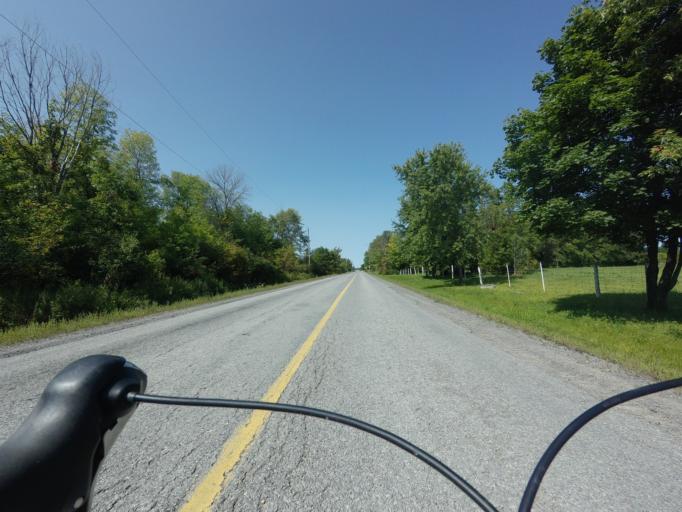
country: CA
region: Ontario
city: Arnprior
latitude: 45.4515
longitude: -76.0855
